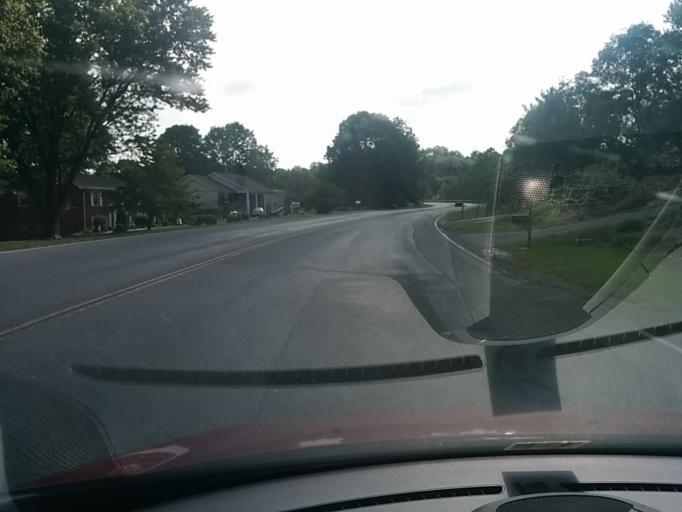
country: US
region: Virginia
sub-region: City of Lexington
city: Lexington
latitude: 37.7693
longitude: -79.4513
